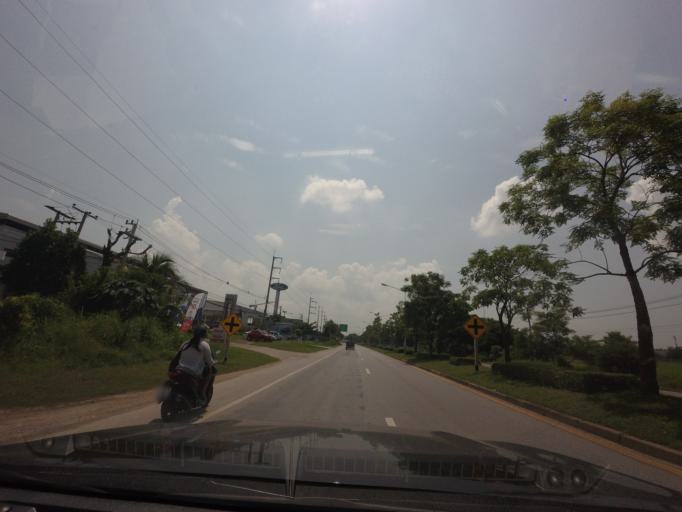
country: TH
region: Uttaradit
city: Uttaradit
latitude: 17.6114
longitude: 100.1234
